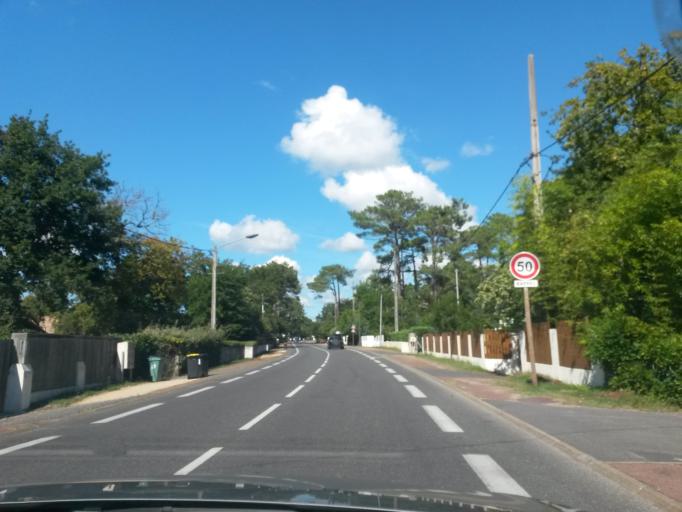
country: FR
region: Aquitaine
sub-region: Departement de la Gironde
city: Arcachon
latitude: 44.7188
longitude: -1.2107
